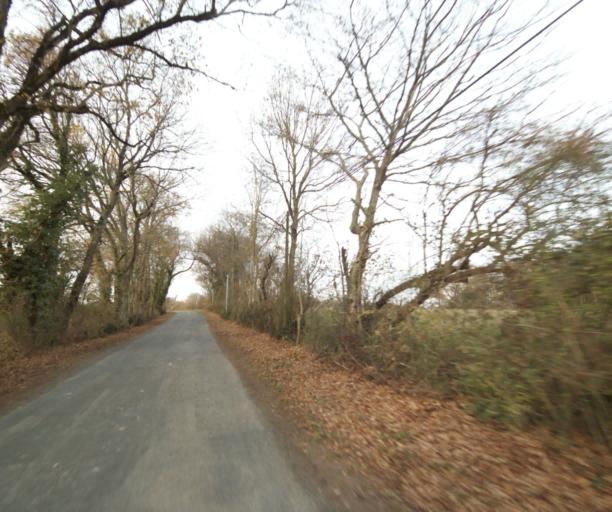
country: FR
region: Poitou-Charentes
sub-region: Departement de la Charente-Maritime
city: Fontcouverte
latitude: 45.7925
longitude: -0.5895
